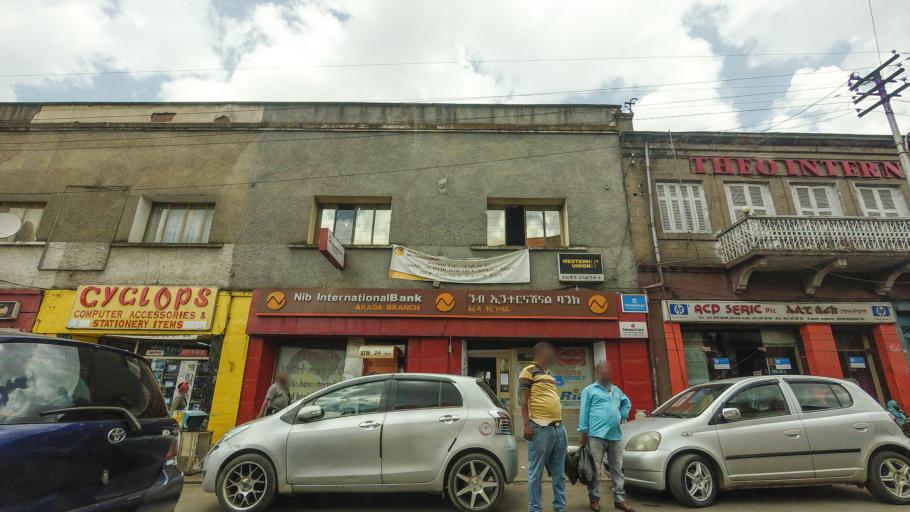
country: ET
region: Adis Abeba
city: Addis Ababa
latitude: 9.0334
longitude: 38.7548
